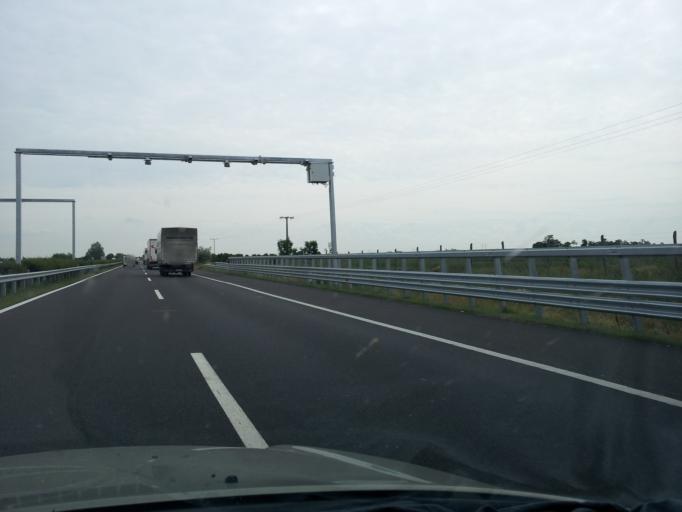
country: HU
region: Heves
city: Karacsond
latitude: 47.7055
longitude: 20.0809
